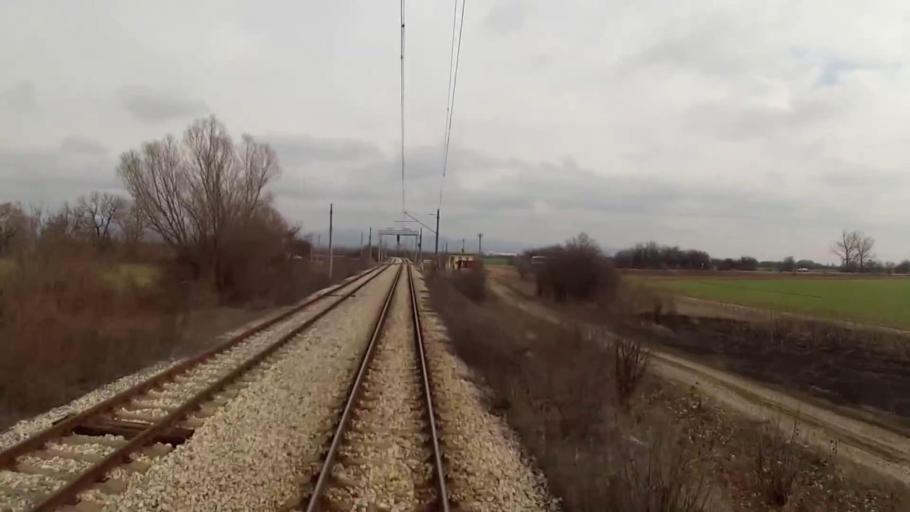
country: BG
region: Sofia-Capital
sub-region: Stolichna Obshtina
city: Bukhovo
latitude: 42.7119
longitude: 23.5662
